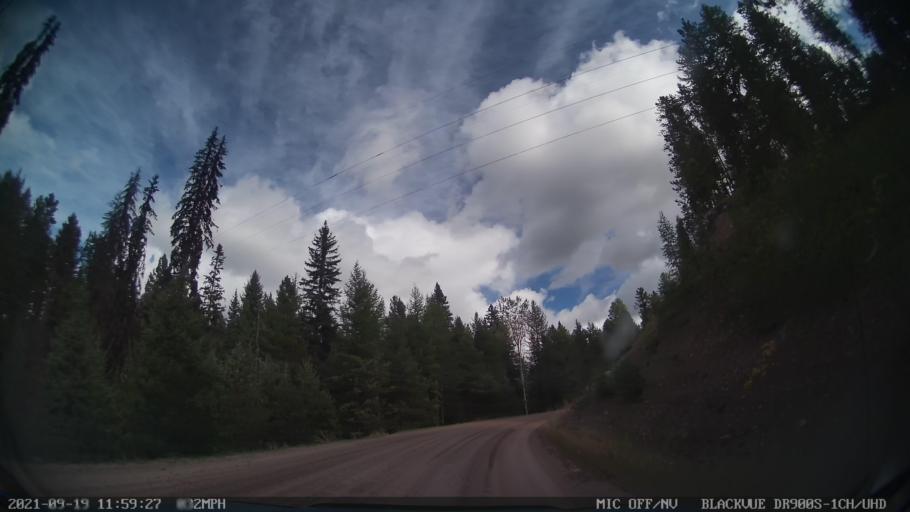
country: US
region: Montana
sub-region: Missoula County
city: Seeley Lake
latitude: 47.1856
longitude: -113.4774
